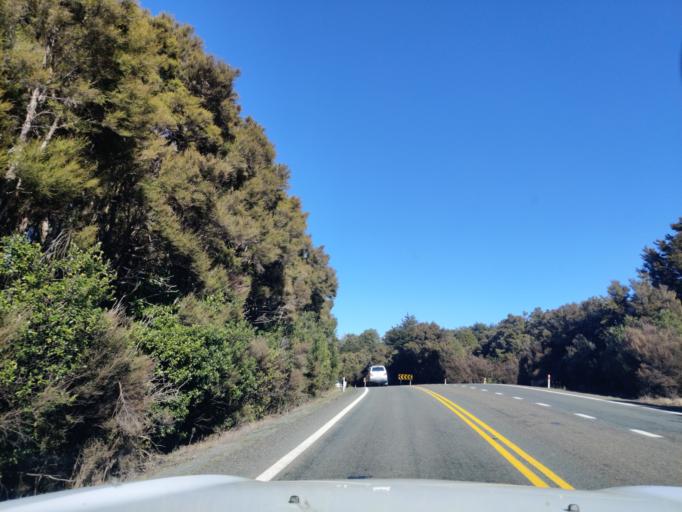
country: NZ
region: Waikato
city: Turangi
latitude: -39.1513
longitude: 175.7680
